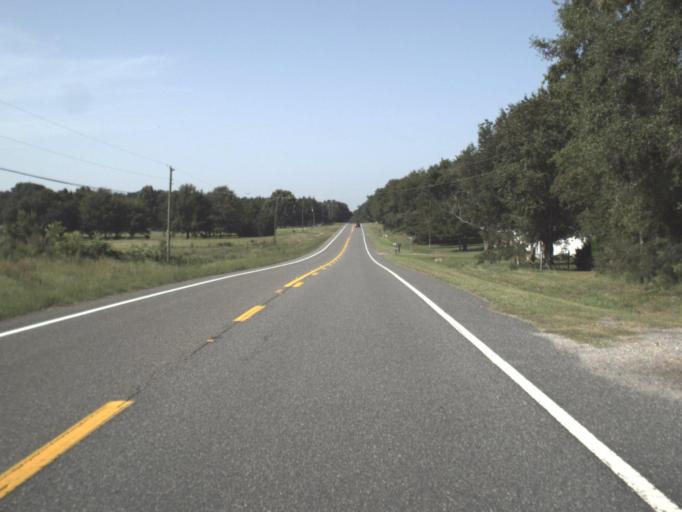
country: US
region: Florida
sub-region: Columbia County
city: Lake City
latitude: 30.0388
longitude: -82.7073
